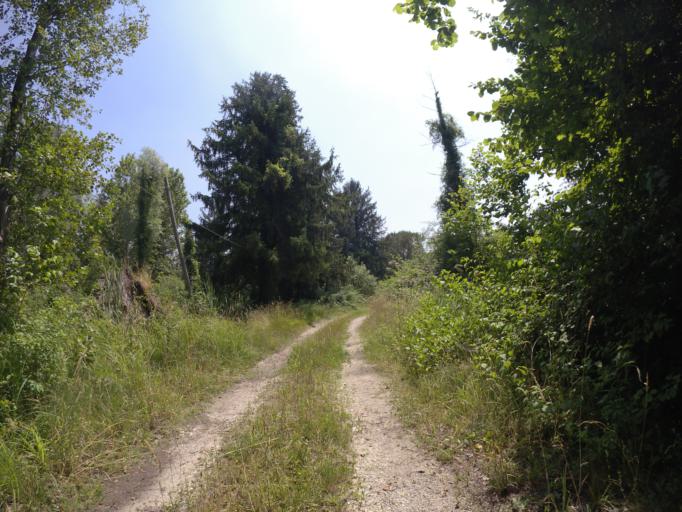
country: IT
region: Friuli Venezia Giulia
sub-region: Provincia di Udine
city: Bertiolo
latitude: 45.9160
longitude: 13.0556
